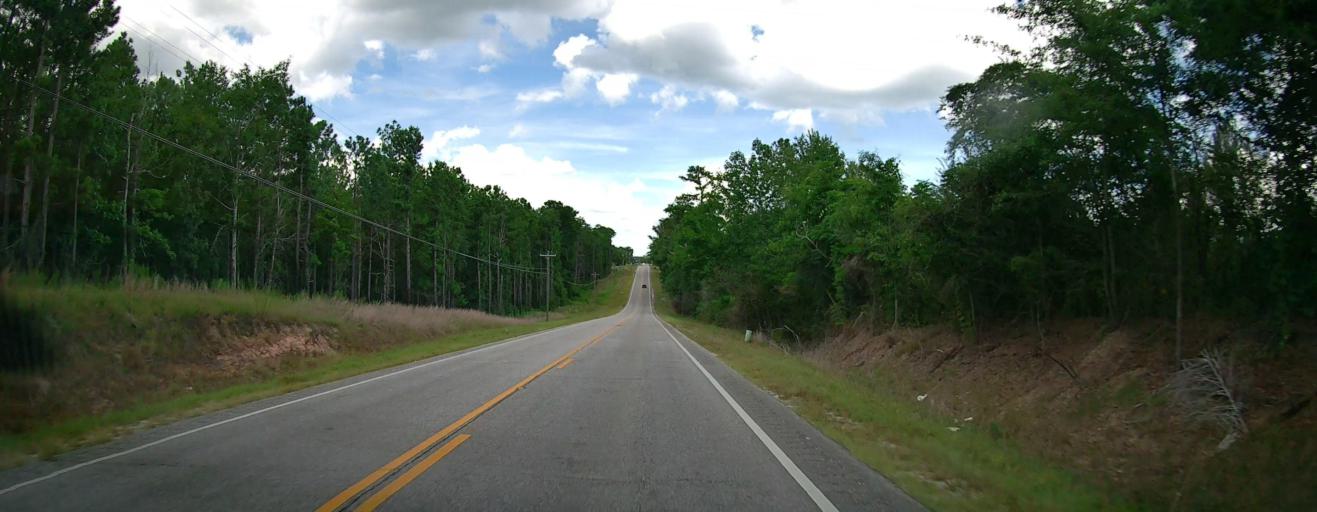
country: US
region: Alabama
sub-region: Macon County
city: Tuskegee
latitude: 32.4658
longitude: -85.5914
